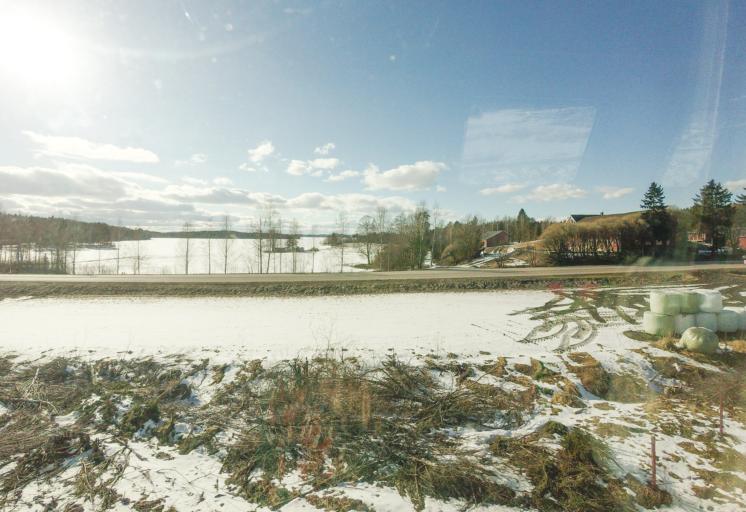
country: FI
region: South Karelia
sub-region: Imatra
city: Parikkala
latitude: 61.4966
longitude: 29.4874
